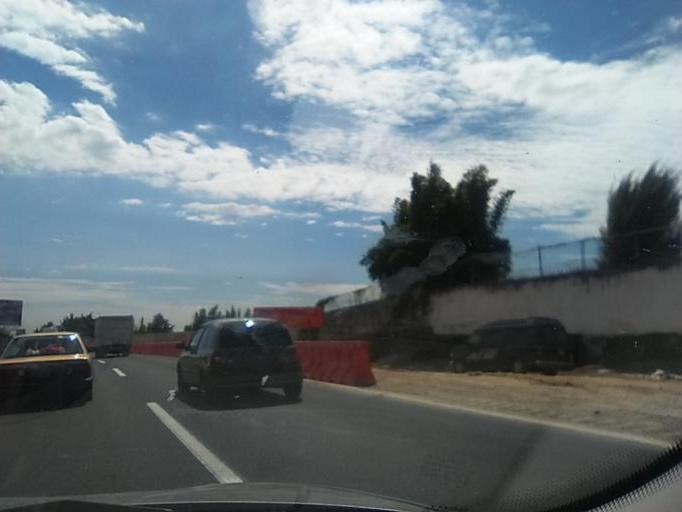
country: MX
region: Morelos
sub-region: Cuernavaca
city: Colonia los Cerritos
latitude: 18.9575
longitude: -99.2237
